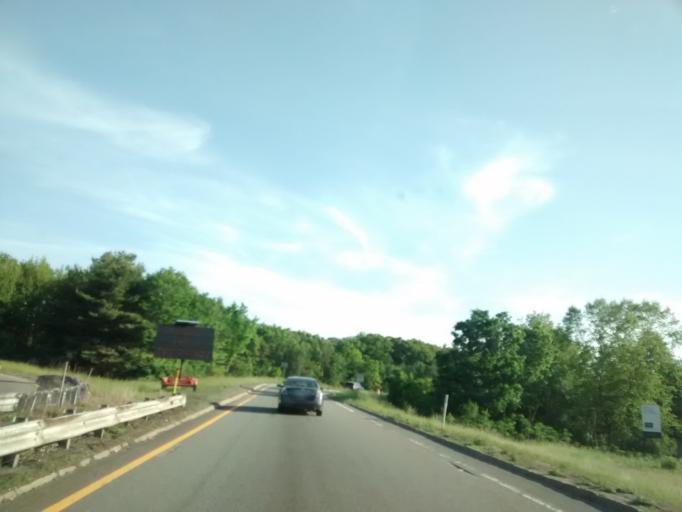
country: US
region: Massachusetts
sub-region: Middlesex County
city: Hudson
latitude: 42.3635
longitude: -71.5936
